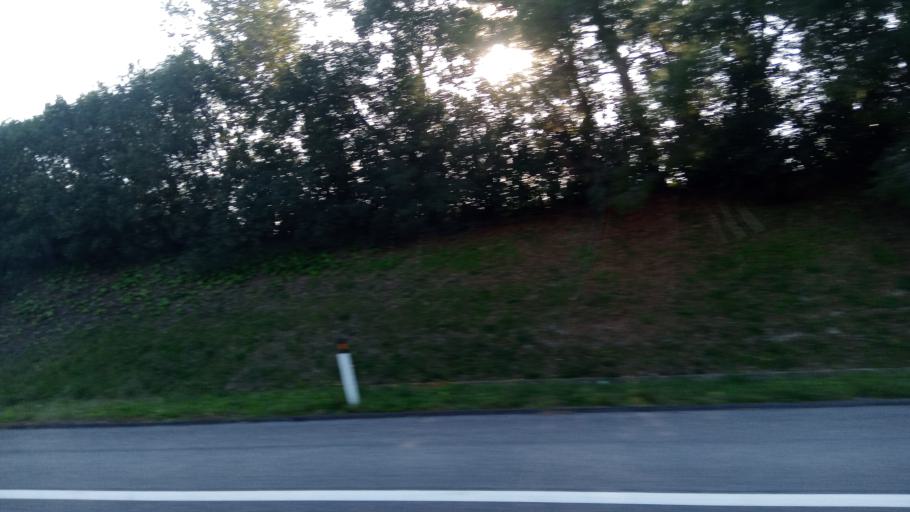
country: IT
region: Molise
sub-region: Provincia di Campobasso
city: Campomarino
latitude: 41.9461
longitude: 15.0283
